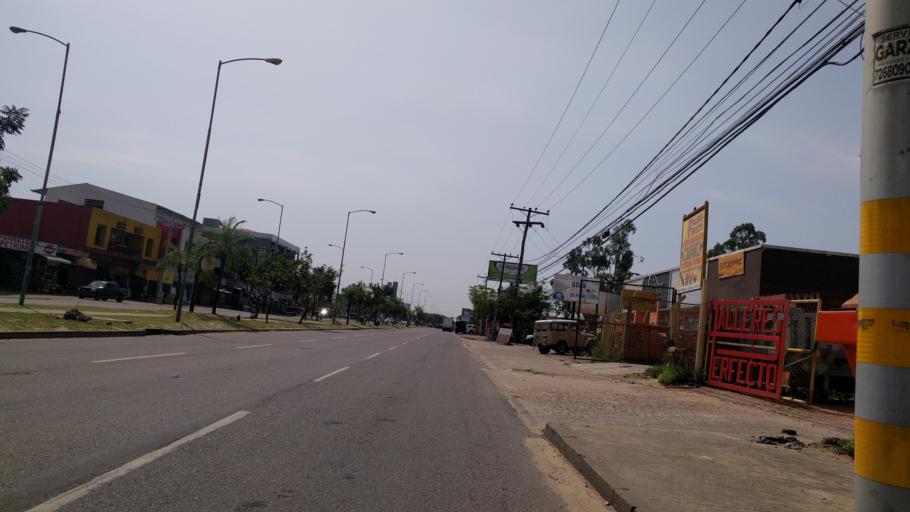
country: BO
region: Santa Cruz
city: Santa Cruz de la Sierra
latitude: -17.8137
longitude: -63.2101
